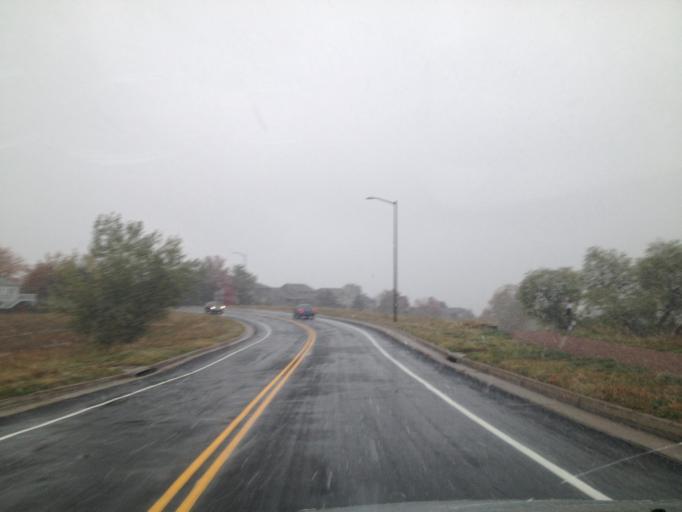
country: US
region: Colorado
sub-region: Boulder County
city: Louisville
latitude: 39.9816
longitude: -105.1553
